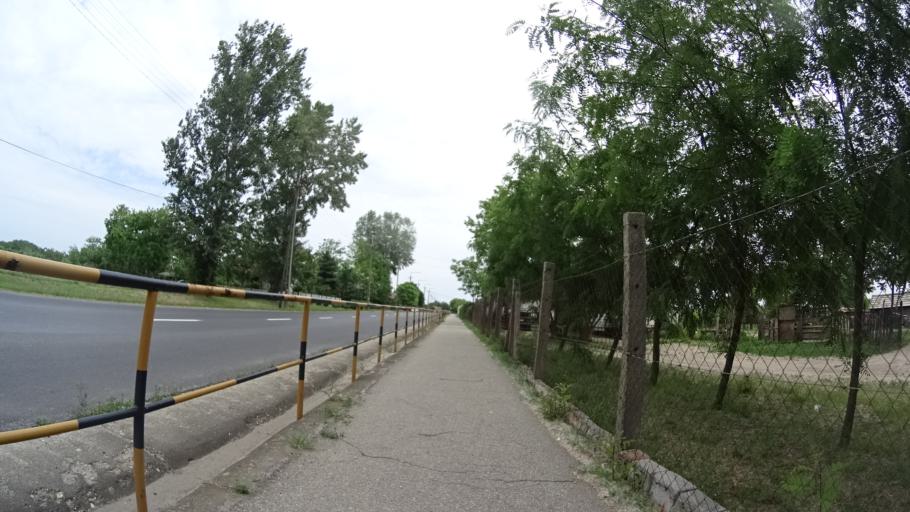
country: HU
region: Bacs-Kiskun
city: Tiszakecske
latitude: 46.9238
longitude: 20.0769
